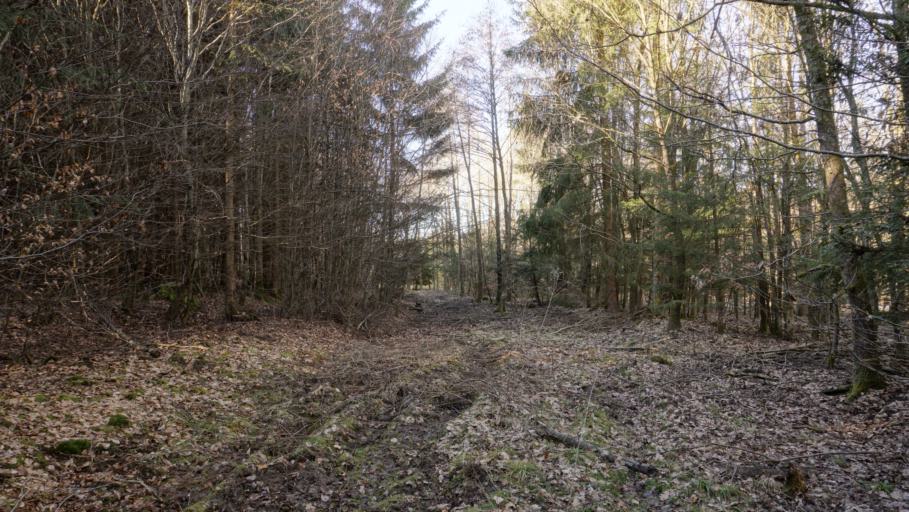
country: DE
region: Baden-Wuerttemberg
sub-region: Karlsruhe Region
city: Fahrenbach
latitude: 49.4095
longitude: 9.1110
